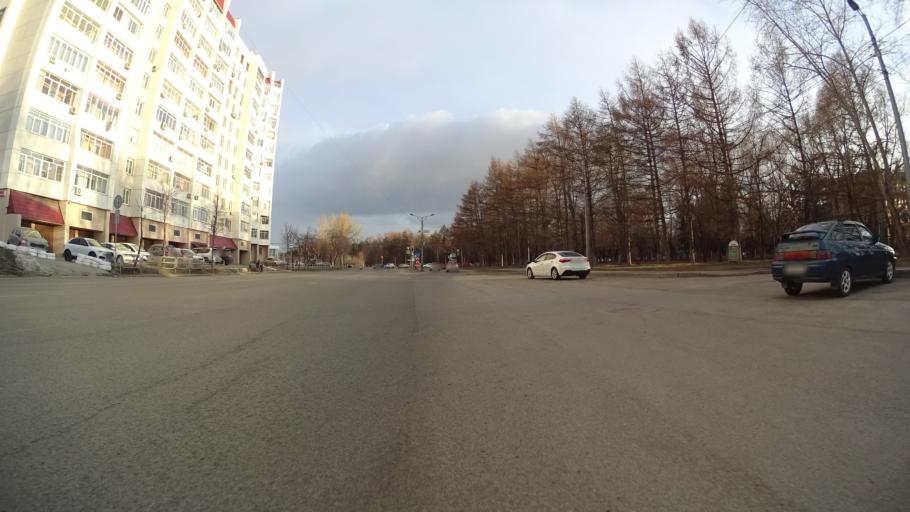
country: RU
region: Chelyabinsk
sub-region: Gorod Chelyabinsk
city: Chelyabinsk
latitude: 55.1484
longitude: 61.3658
